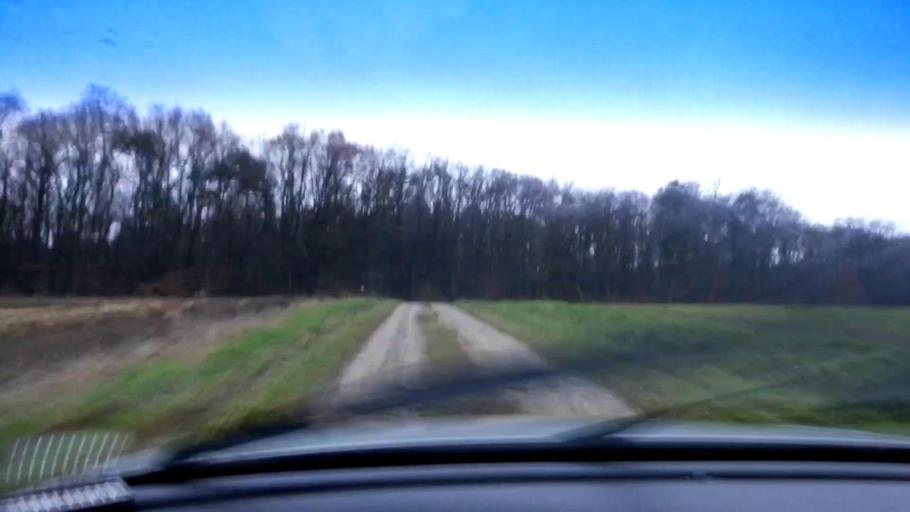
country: DE
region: Bavaria
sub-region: Upper Franconia
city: Schesslitz
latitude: 49.9913
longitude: 10.9921
